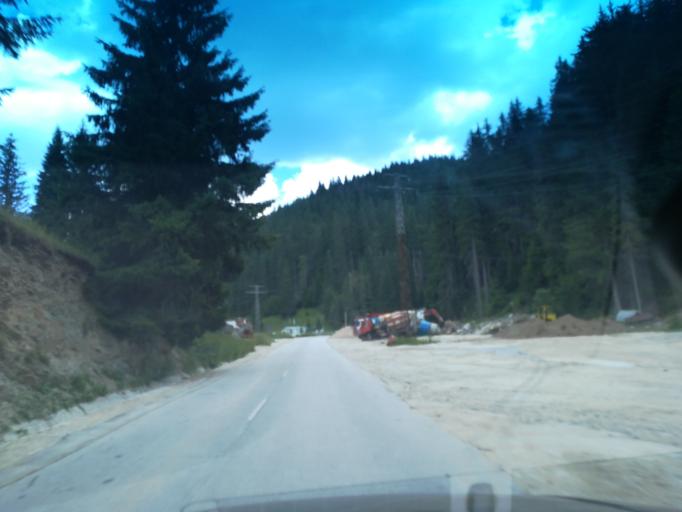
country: BG
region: Smolyan
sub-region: Obshtina Chepelare
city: Chepelare
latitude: 41.6613
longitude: 24.6774
